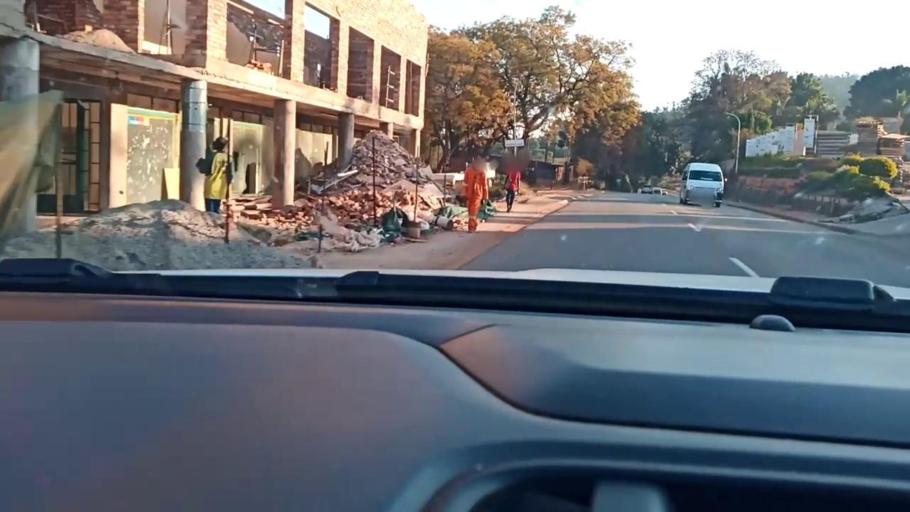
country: ZA
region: Limpopo
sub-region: Mopani District Municipality
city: Duiwelskloof
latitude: -23.6978
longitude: 30.1384
